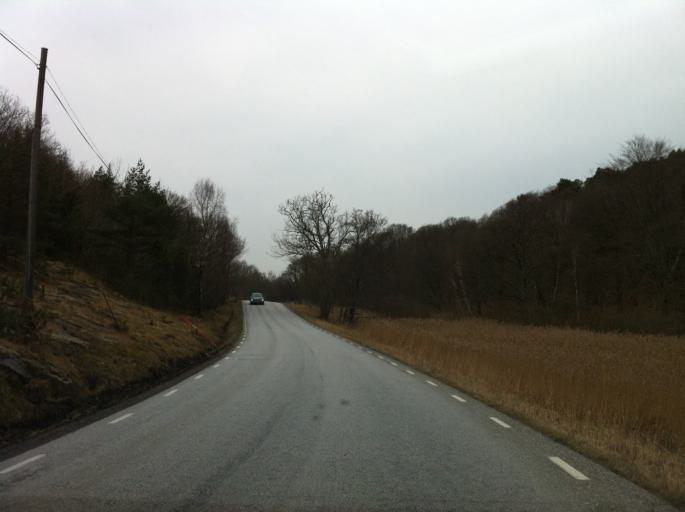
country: SE
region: Vaestra Goetaland
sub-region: Orust
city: Henan
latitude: 58.2633
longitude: 11.6820
